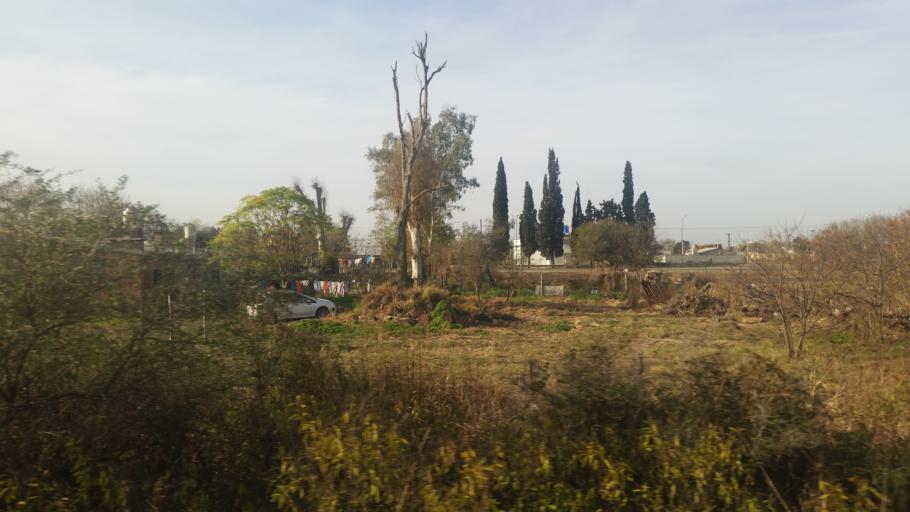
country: AR
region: Cordoba
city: Toledo
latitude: -31.5599
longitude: -64.0055
